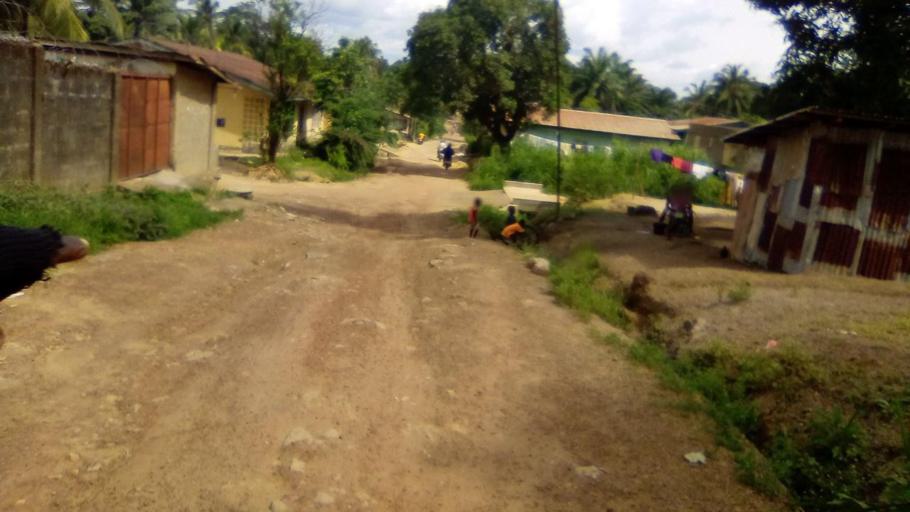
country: SL
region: Southern Province
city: Bo
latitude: 7.9589
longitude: -11.7210
